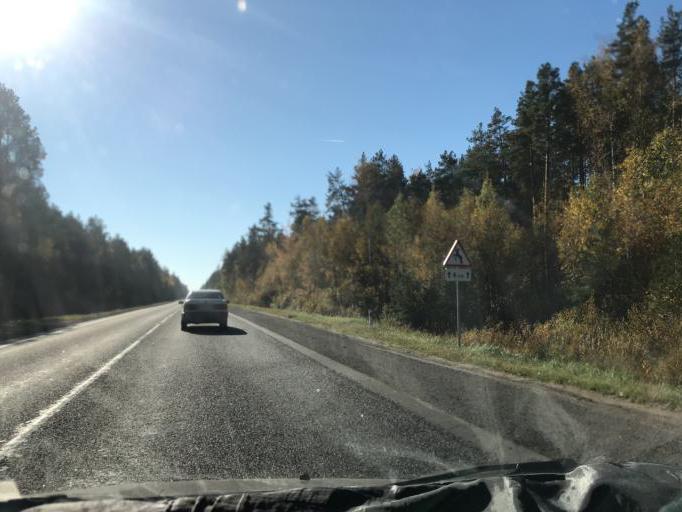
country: BY
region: Mogilev
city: Babruysk
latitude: 53.1641
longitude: 29.0456
